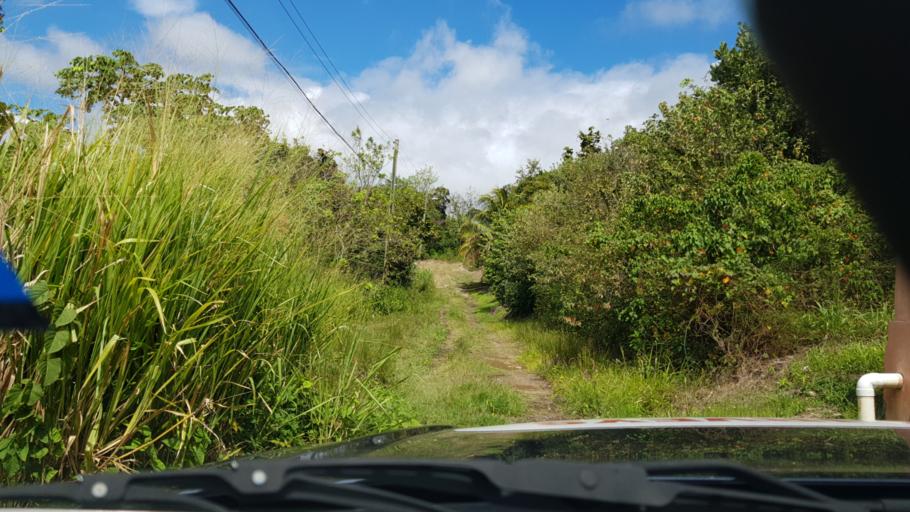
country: LC
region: Anse-la-Raye
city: Anse La Raye
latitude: 13.9457
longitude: -61.0362
